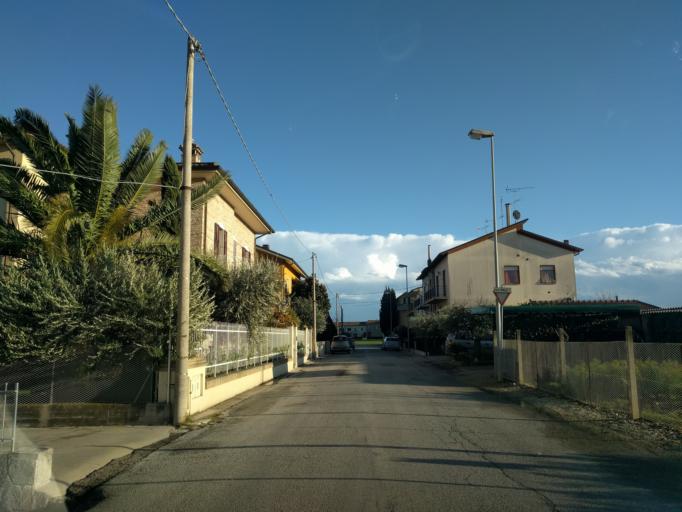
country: IT
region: The Marches
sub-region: Provincia di Pesaro e Urbino
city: Bellocchi
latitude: 43.7971
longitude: 13.0009
